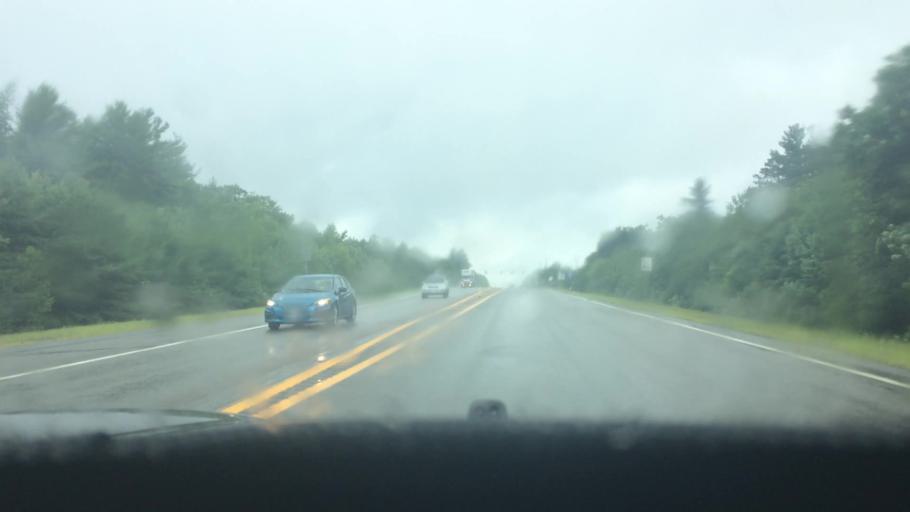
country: US
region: Massachusetts
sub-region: Worcester County
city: South Ashburnham
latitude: 42.5889
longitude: -71.9588
